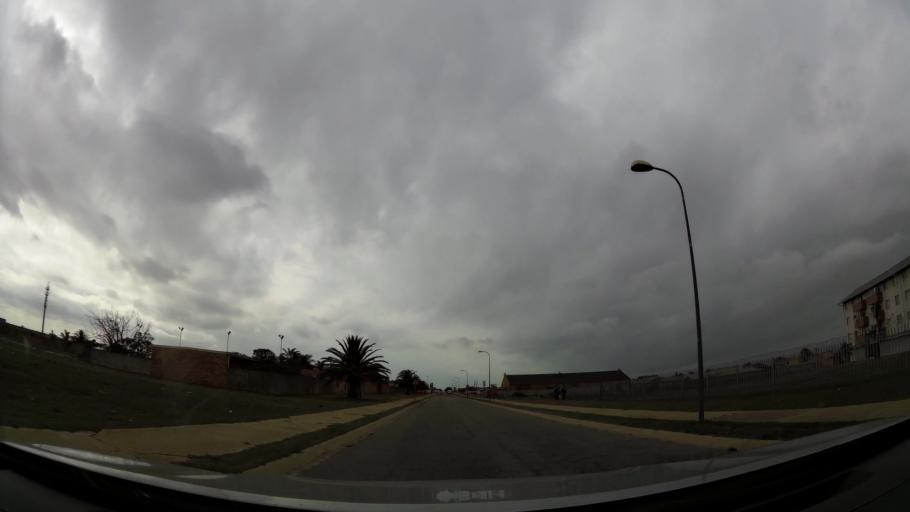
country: ZA
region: Eastern Cape
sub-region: Nelson Mandela Bay Metropolitan Municipality
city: Port Elizabeth
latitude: -33.9038
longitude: 25.5590
